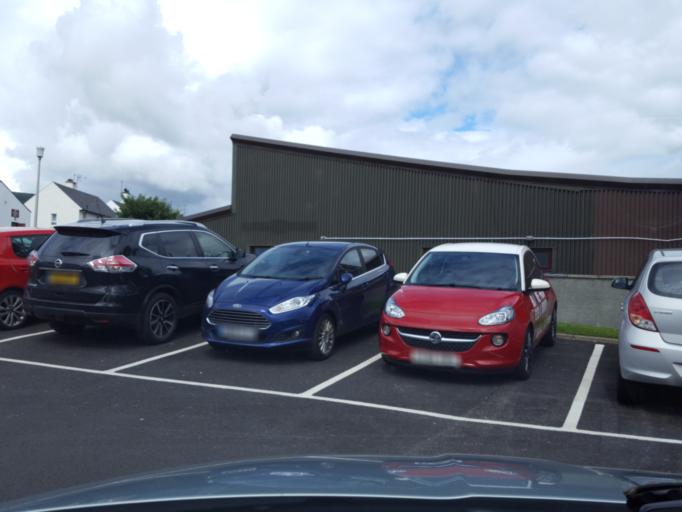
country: GB
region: Scotland
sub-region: Highland
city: Aviemore
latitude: 57.1923
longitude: -3.8279
